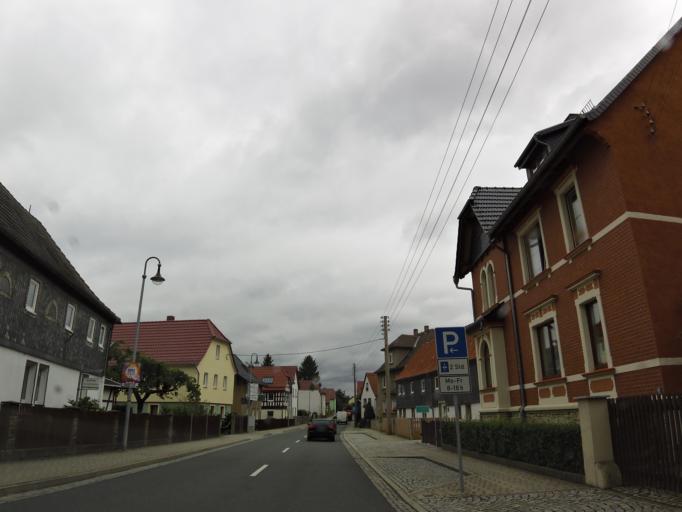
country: DE
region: Thuringia
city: Bad Klosterlausnitz
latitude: 50.9190
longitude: 11.8691
